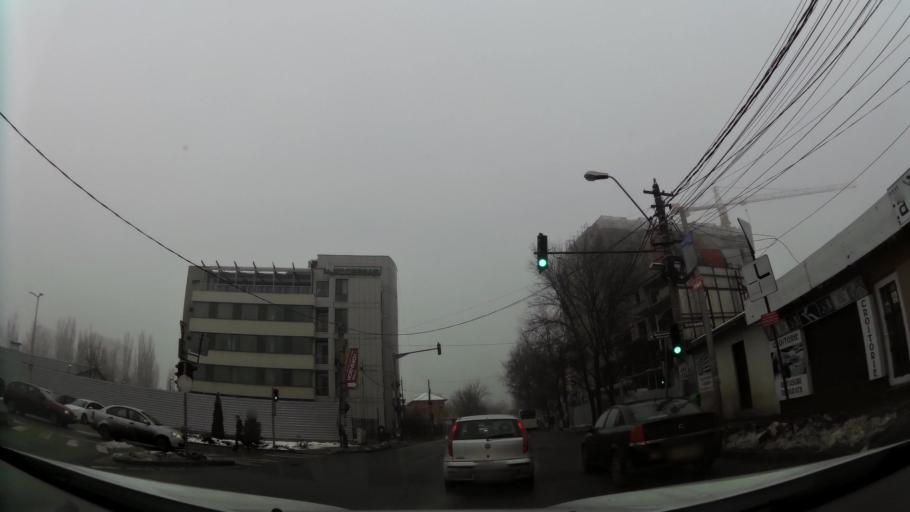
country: RO
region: Ilfov
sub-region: Comuna Chiajna
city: Rosu
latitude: 44.4438
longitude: 26.0195
